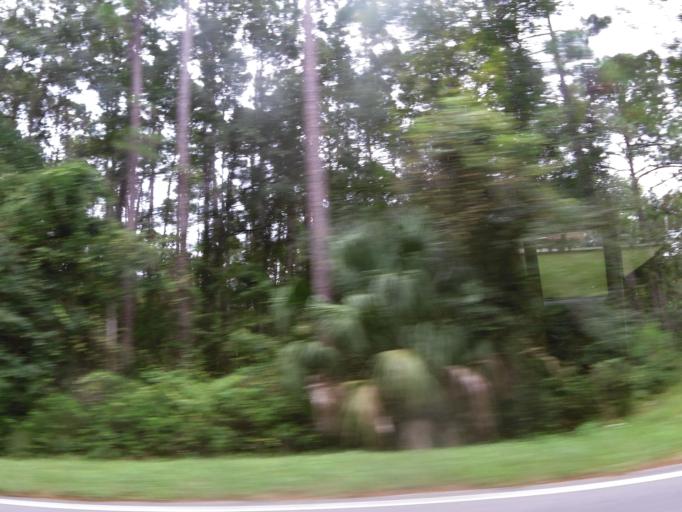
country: US
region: Florida
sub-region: Clay County
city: Bellair-Meadowbrook Terrace
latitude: 30.2273
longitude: -81.7729
